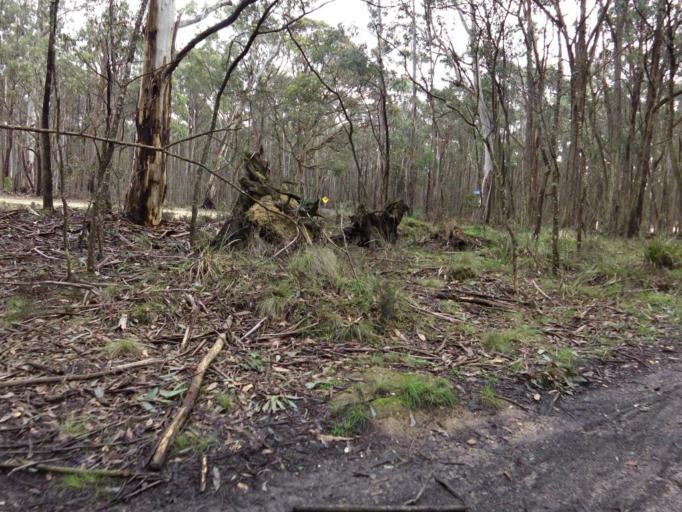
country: AU
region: Victoria
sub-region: Moorabool
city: Bacchus Marsh
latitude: -37.4109
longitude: 144.4922
